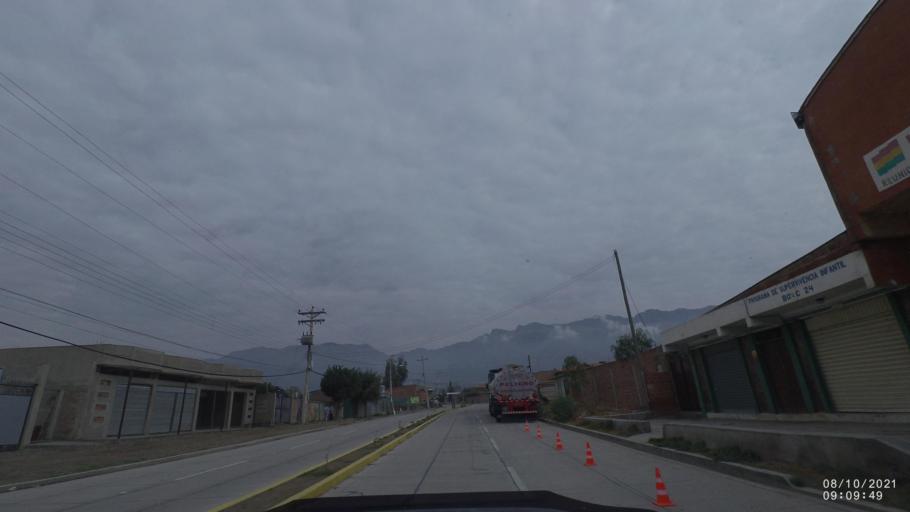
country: BO
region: Cochabamba
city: Sipe Sipe
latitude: -17.3942
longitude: -66.3294
